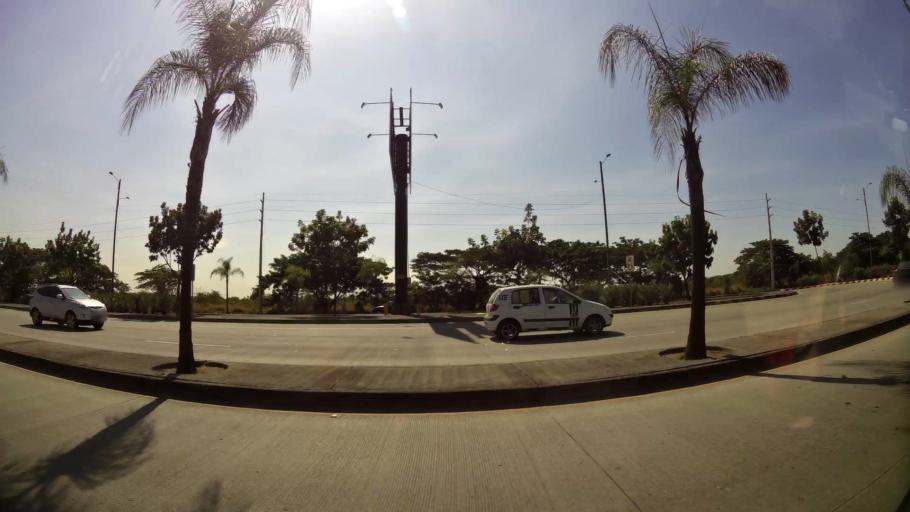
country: EC
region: Guayas
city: Eloy Alfaro
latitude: -2.1133
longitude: -79.8848
